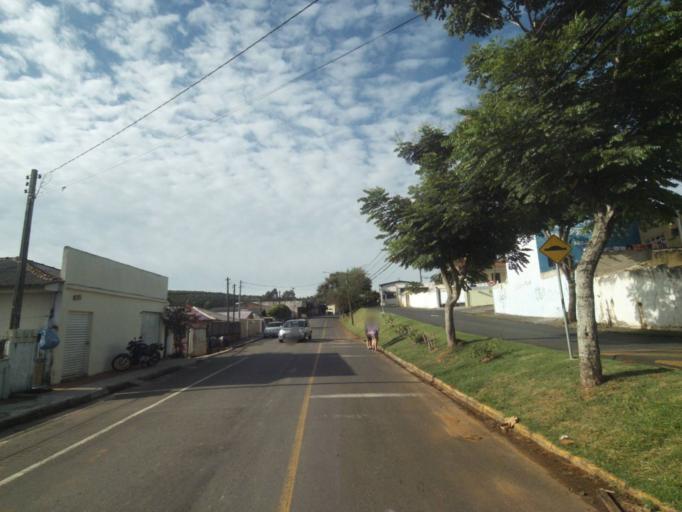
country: BR
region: Parana
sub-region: Telemaco Borba
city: Telemaco Borba
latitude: -24.3465
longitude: -50.6124
